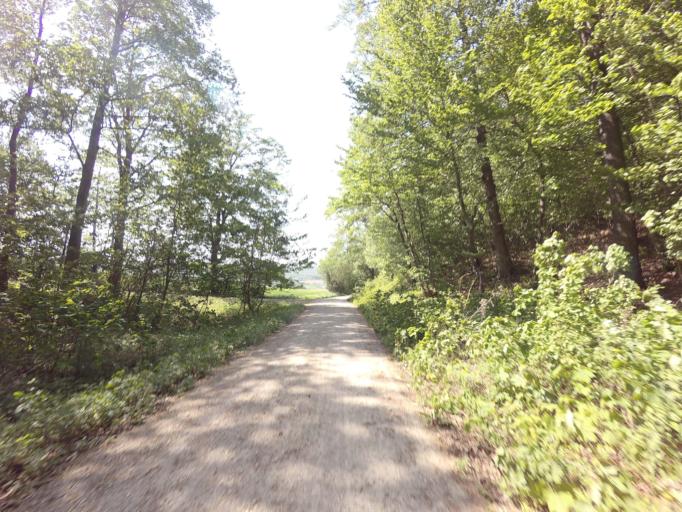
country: DE
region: Lower Saxony
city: Diekholzen
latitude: 52.1360
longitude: 9.8939
